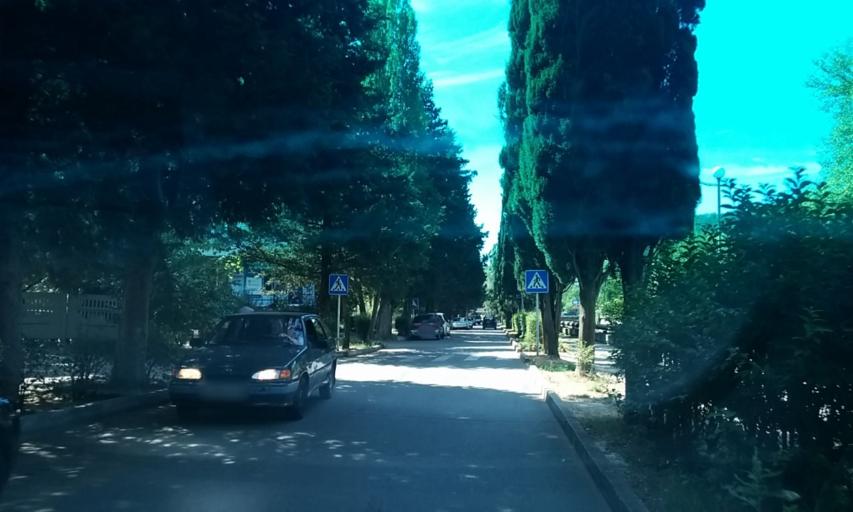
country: RU
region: Krasnodarskiy
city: Tuapse
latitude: 44.1083
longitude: 39.0607
